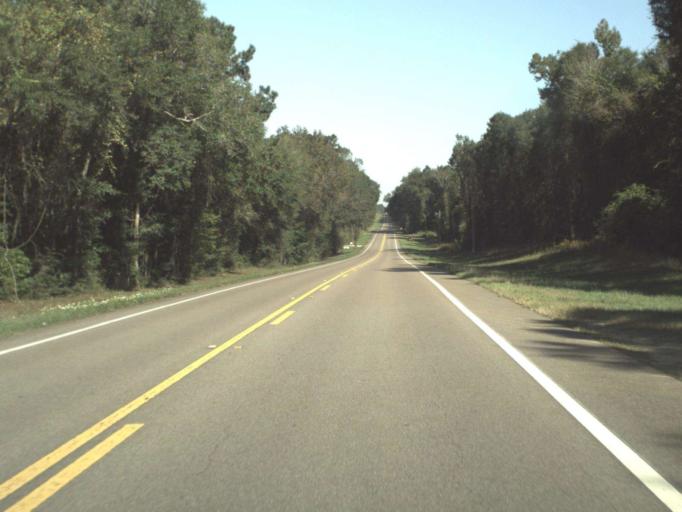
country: US
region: Florida
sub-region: Walton County
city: DeFuniak Springs
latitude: 30.6710
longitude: -85.9365
